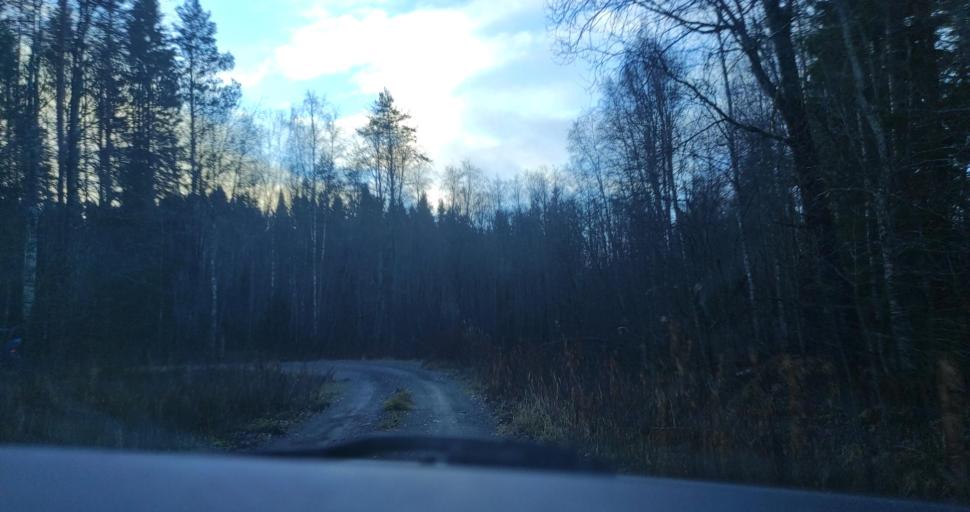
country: RU
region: Republic of Karelia
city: Pitkyaranta
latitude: 61.7336
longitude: 31.3731
